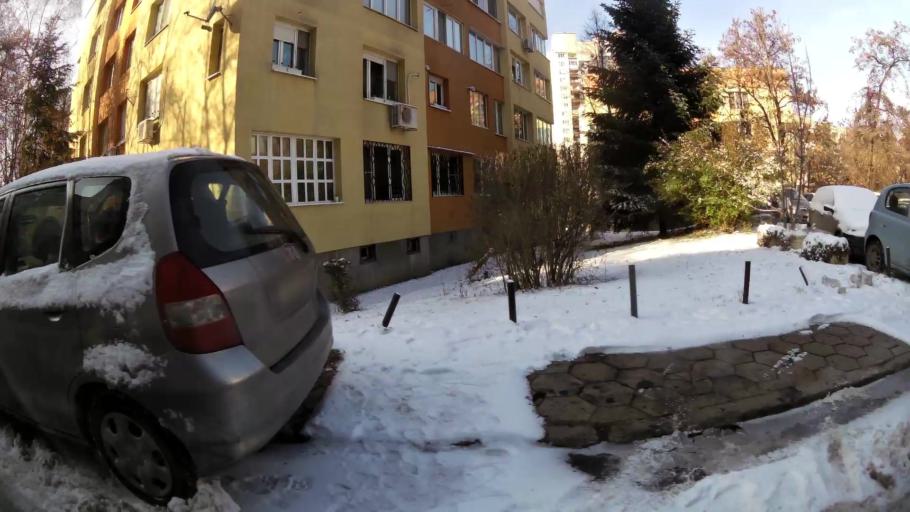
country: BG
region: Sofia-Capital
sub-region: Stolichna Obshtina
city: Sofia
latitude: 42.6591
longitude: 23.3429
